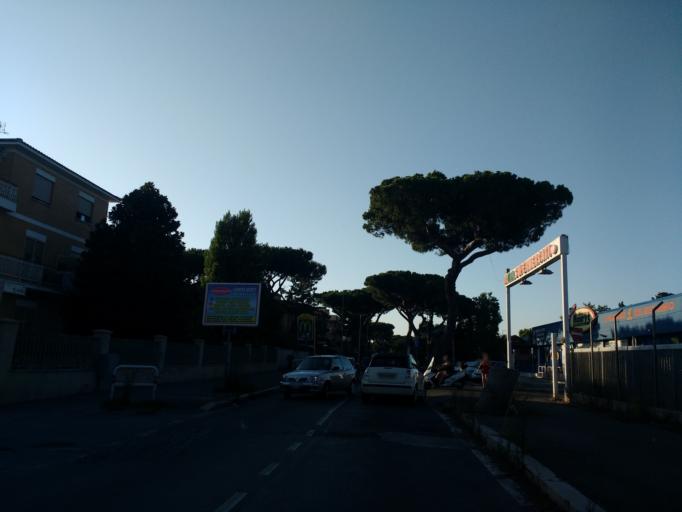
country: IT
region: Latium
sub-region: Citta metropolitana di Roma Capitale
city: Acilia-Castel Fusano-Ostia Antica
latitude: 41.7786
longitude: 12.3681
